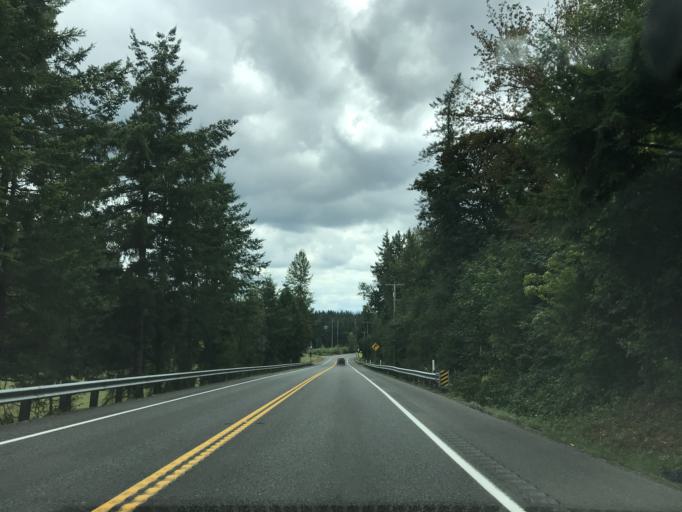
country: US
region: Washington
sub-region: King County
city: Maple Valley
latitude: 47.4019
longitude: -122.0473
